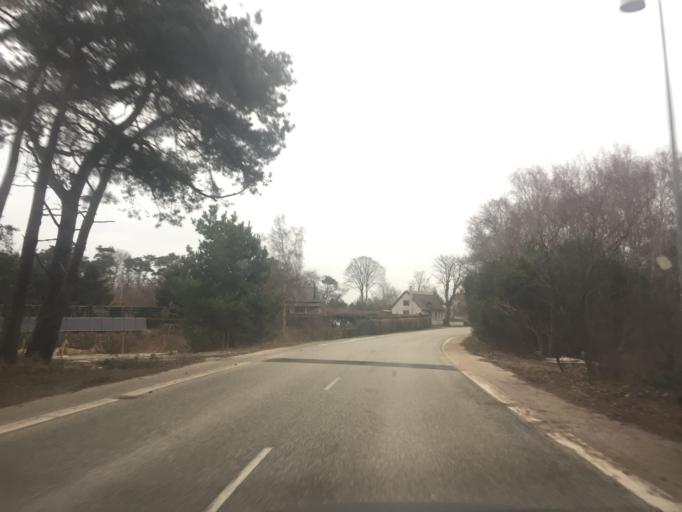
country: DK
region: Capital Region
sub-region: Halsnaes Kommune
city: Liseleje
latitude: 56.0006
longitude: 11.9750
